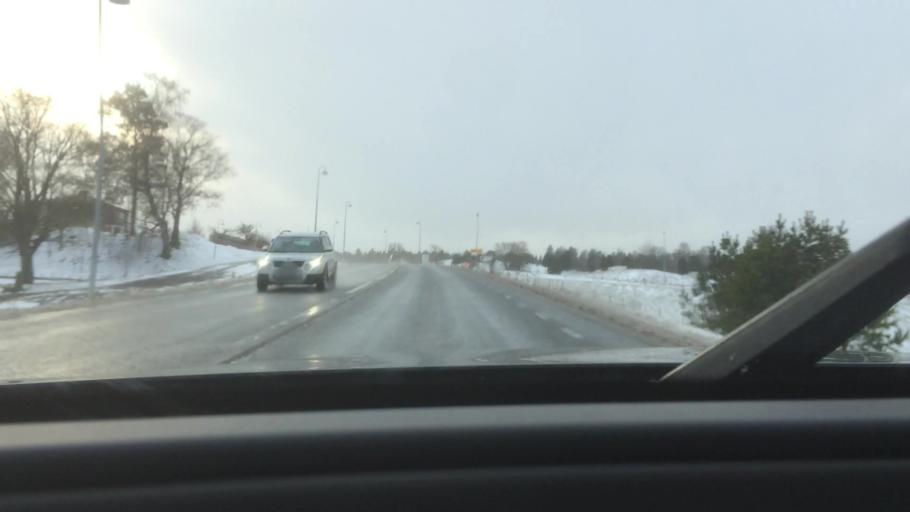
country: SE
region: Vaestra Goetaland
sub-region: Falkopings Kommun
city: Falkoeping
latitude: 57.9811
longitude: 13.5284
